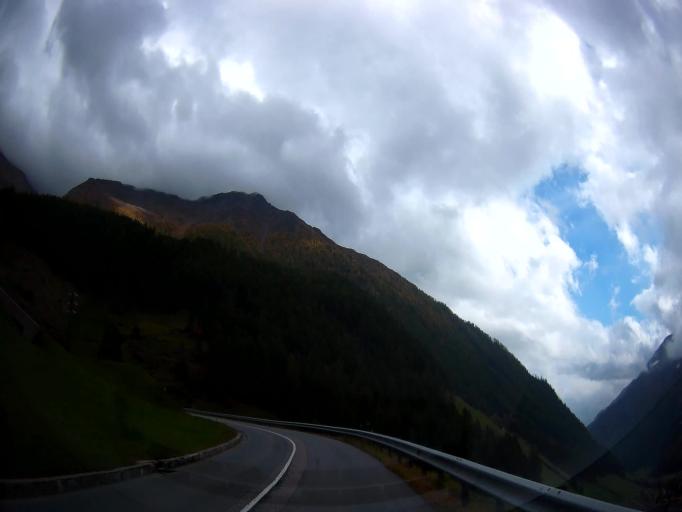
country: IT
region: Trentino-Alto Adige
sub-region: Bolzano
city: Senales
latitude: 46.7316
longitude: 10.8533
